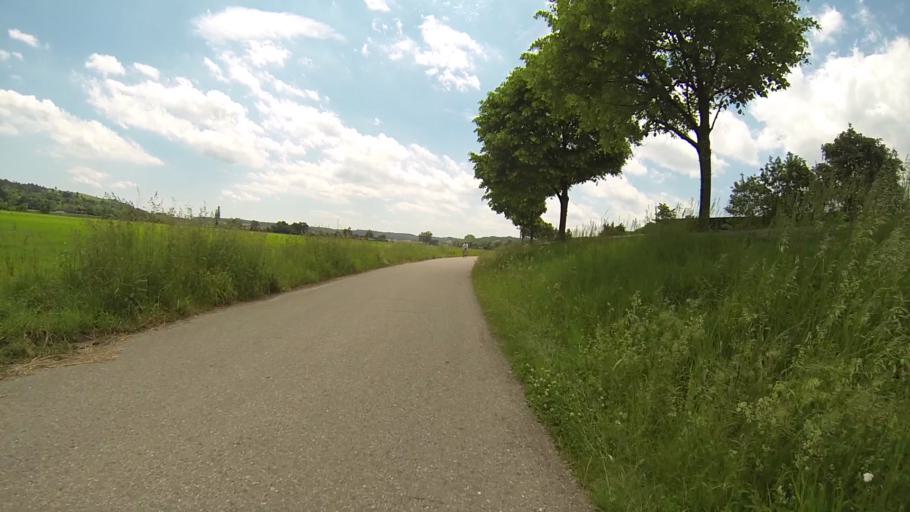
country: DE
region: Baden-Wuerttemberg
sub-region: Regierungsbezirk Stuttgart
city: Bolheim
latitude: 48.6452
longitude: 10.1606
